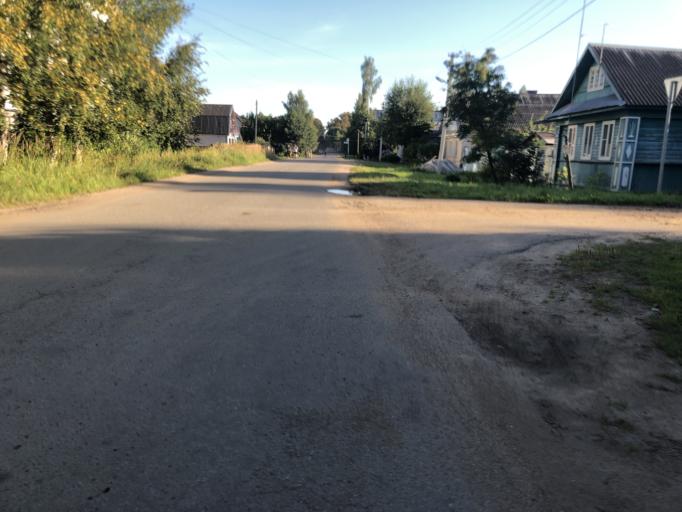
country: RU
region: Tverskaya
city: Rzhev
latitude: 56.2451
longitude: 34.3345
